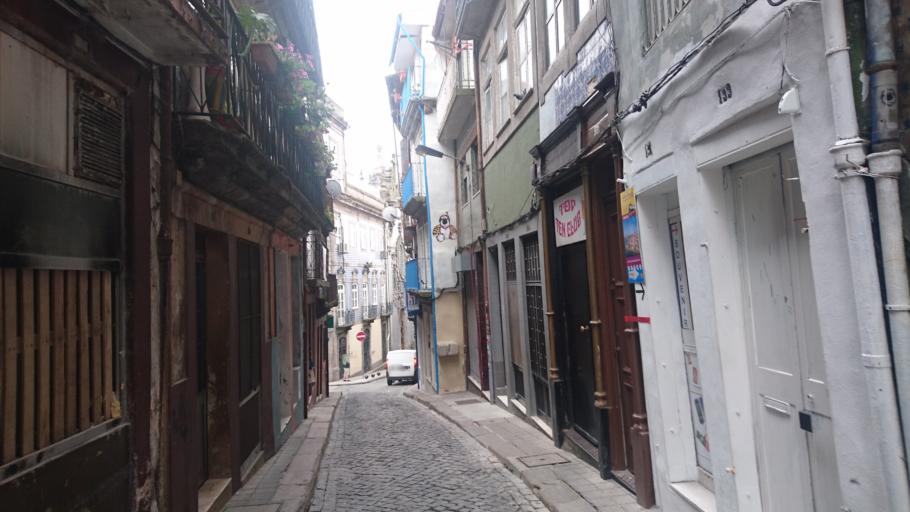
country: PT
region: Porto
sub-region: Porto
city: Porto
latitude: 41.1452
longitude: -8.6078
